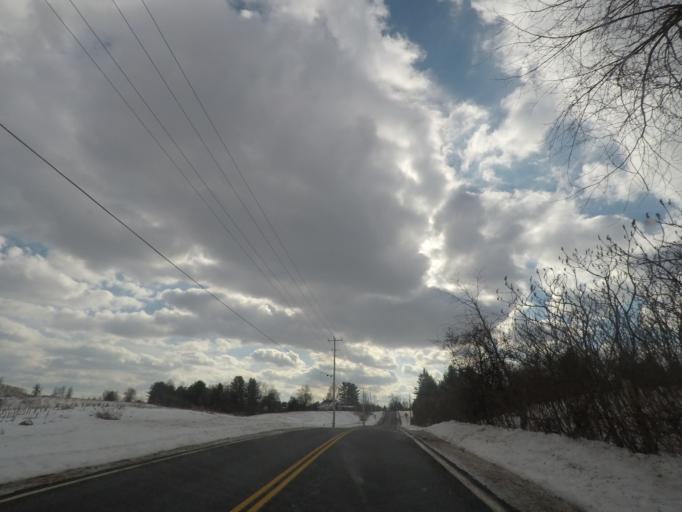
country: US
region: New York
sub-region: Saratoga County
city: Mechanicville
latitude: 42.9062
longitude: -73.7461
